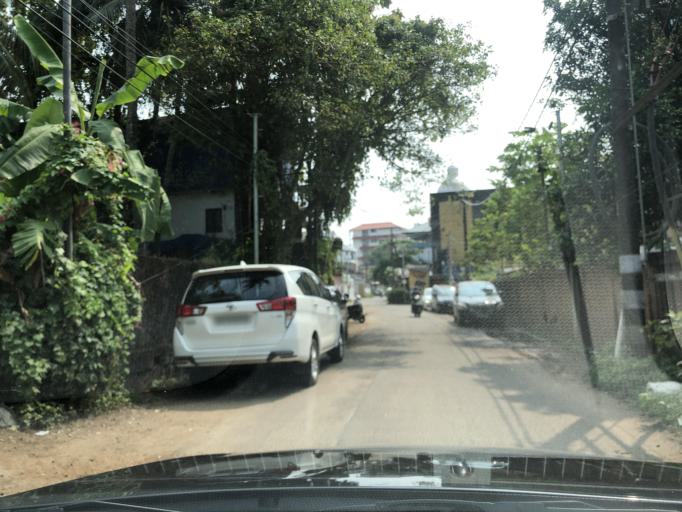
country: IN
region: Kerala
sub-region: Kozhikode
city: Kozhikode
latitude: 11.2544
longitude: 75.7741
